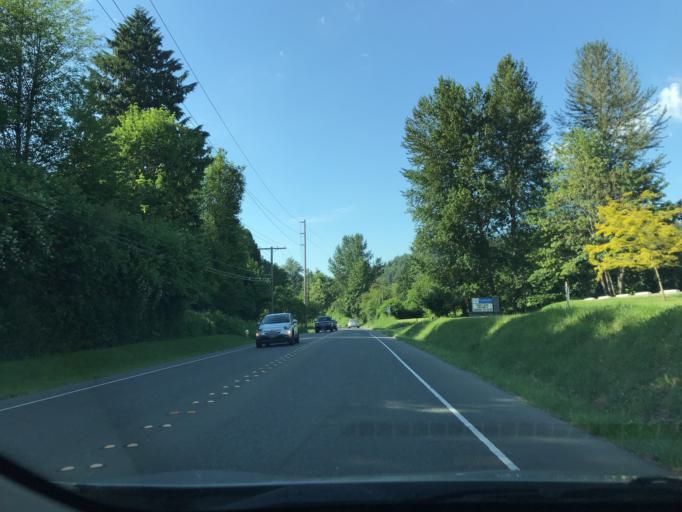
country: US
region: Washington
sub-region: King County
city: Issaquah
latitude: 47.5108
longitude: -122.0232
